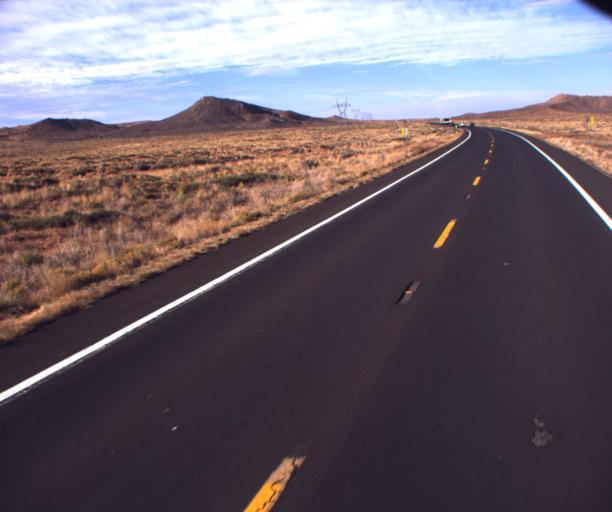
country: US
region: Arizona
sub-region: Apache County
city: Lukachukai
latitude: 36.9636
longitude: -109.4805
